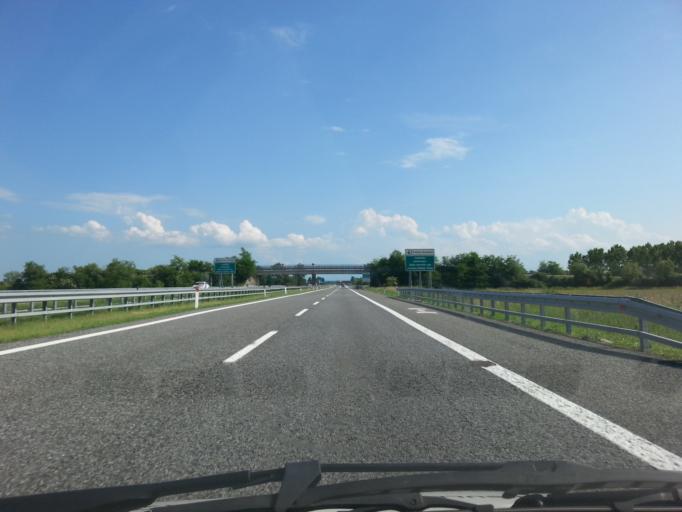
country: IT
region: Piedmont
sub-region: Provincia di Cuneo
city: Marene
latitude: 44.6801
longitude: 7.7698
